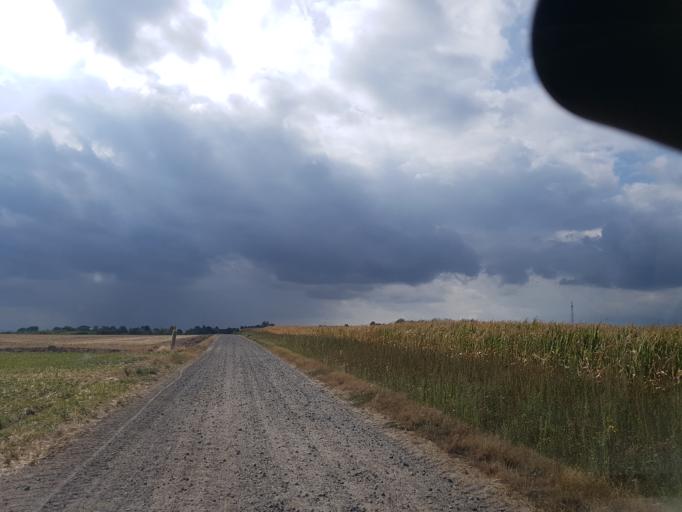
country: DE
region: Brandenburg
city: Treuenbrietzen
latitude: 52.0097
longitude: 12.8321
